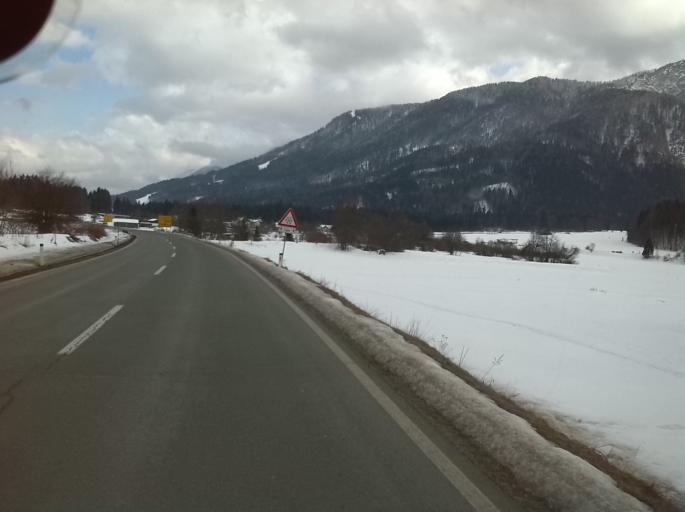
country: AT
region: Carinthia
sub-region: Politischer Bezirk Villach Land
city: Arnoldstein
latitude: 46.4948
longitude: 13.7153
